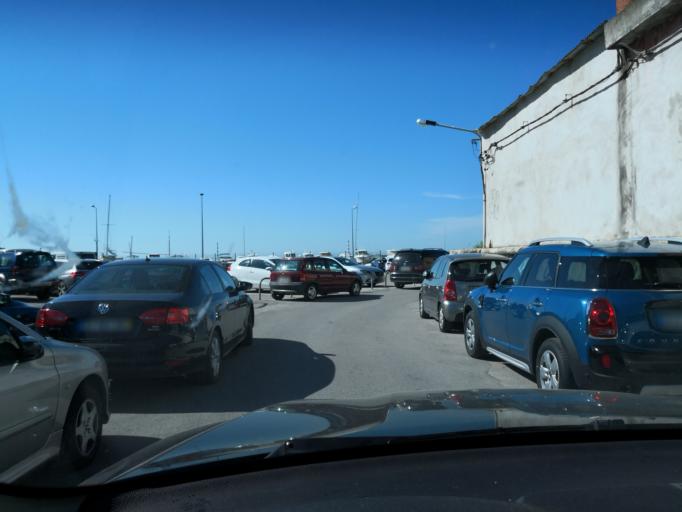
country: PT
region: Setubal
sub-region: Setubal
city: Setubal
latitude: 38.5217
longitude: -8.8933
